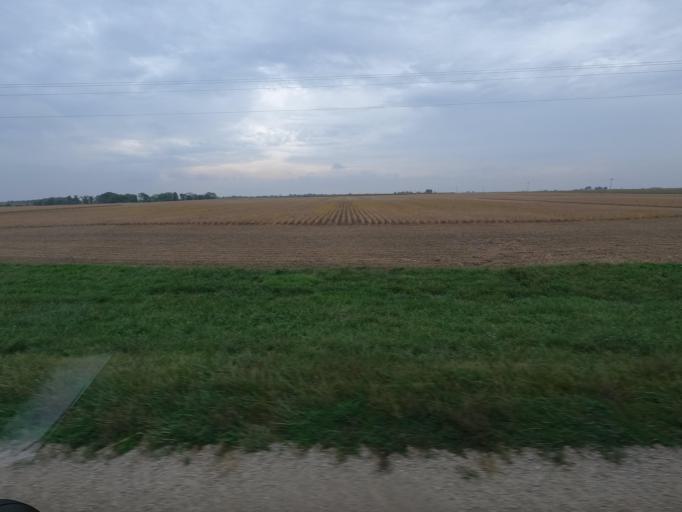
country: US
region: Iowa
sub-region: Henry County
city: Mount Pleasant
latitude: 40.8047
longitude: -91.7042
